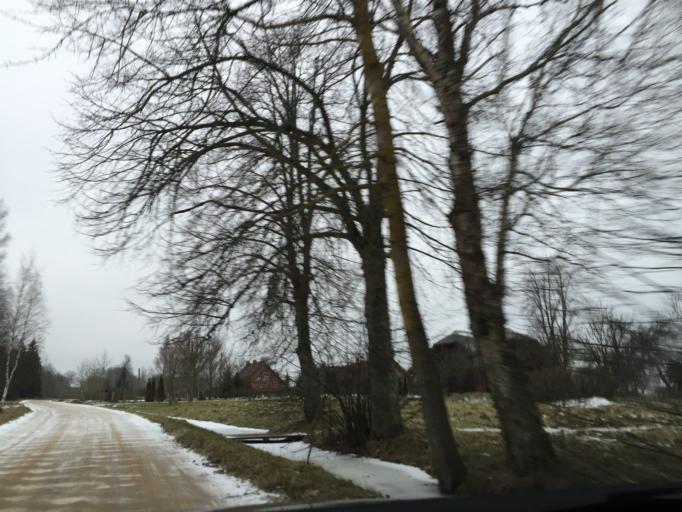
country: LV
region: Salacgrivas
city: Salacgriva
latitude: 57.5117
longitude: 24.3822
